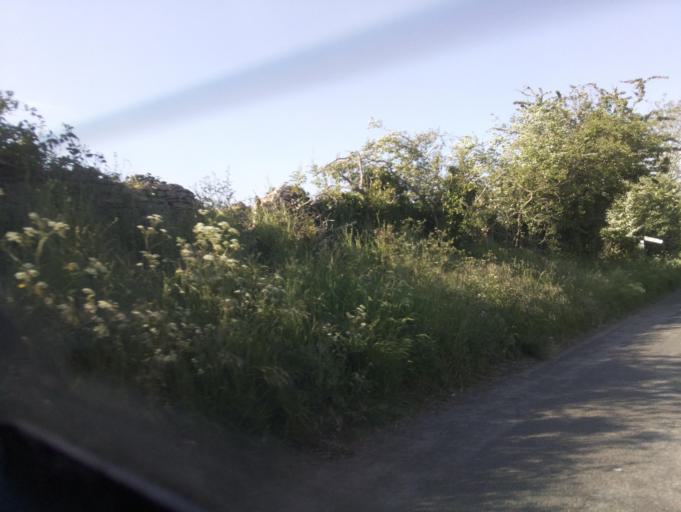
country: GB
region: England
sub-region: Wiltshire
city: Nettleton
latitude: 51.5088
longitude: -2.2919
